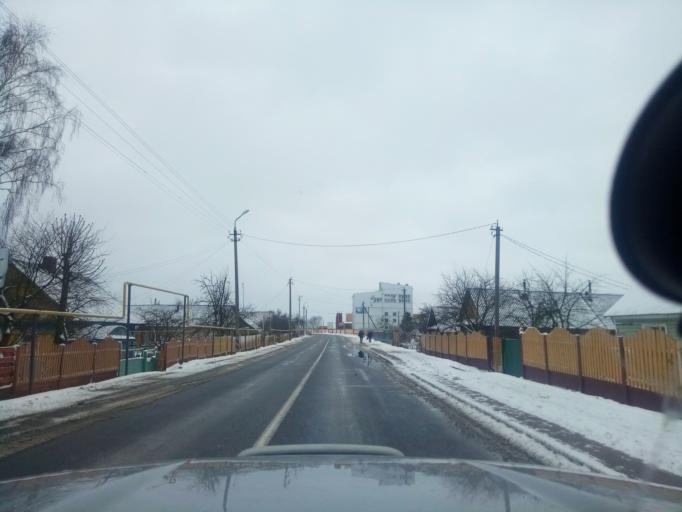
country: BY
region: Minsk
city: Kapyl'
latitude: 53.1439
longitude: 27.0932
